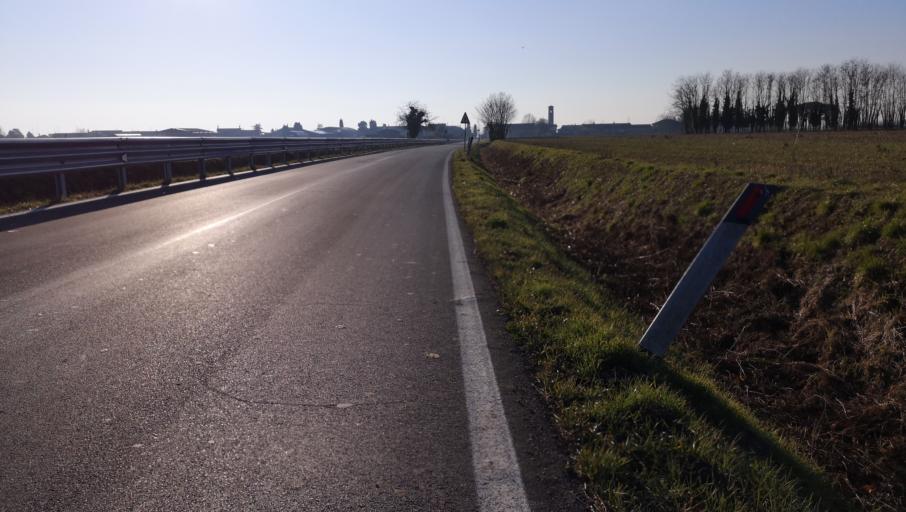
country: IT
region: Friuli Venezia Giulia
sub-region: Provincia di Udine
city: Percoto
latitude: 45.9546
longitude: 13.3074
